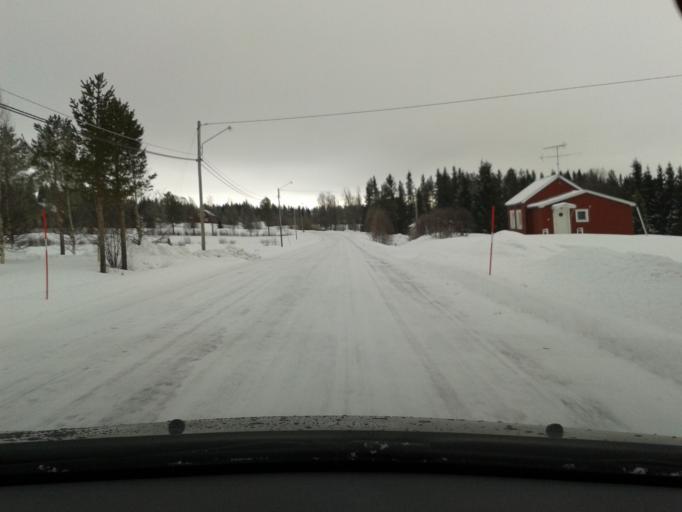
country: SE
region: Vaesterbotten
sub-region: Vilhelmina Kommun
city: Sjoberg
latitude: 64.8343
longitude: 15.9303
